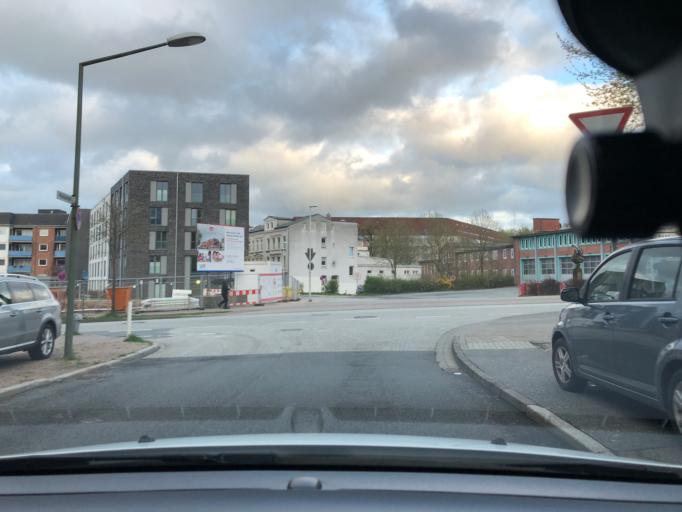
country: DE
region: Schleswig-Holstein
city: Flensburg
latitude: 54.7784
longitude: 9.4377
